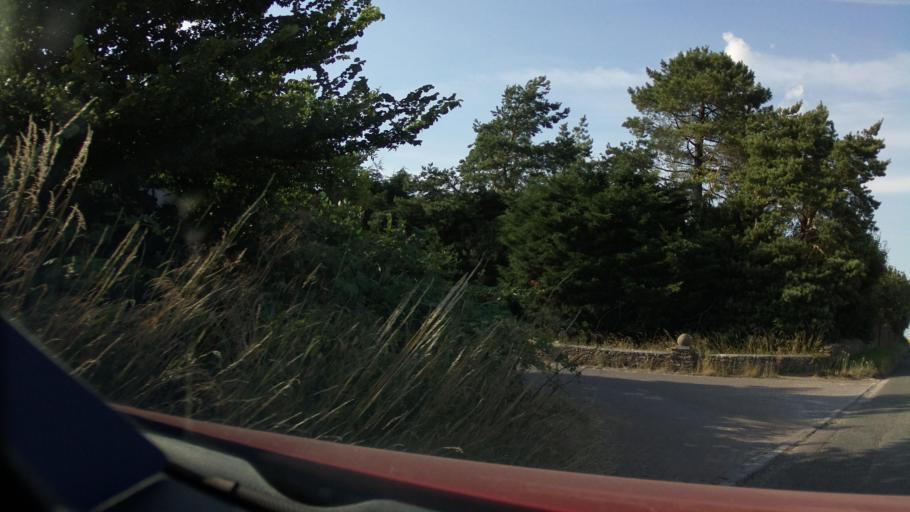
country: GB
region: England
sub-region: South Gloucestershire
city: Marshfield
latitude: 51.4703
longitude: -2.3127
